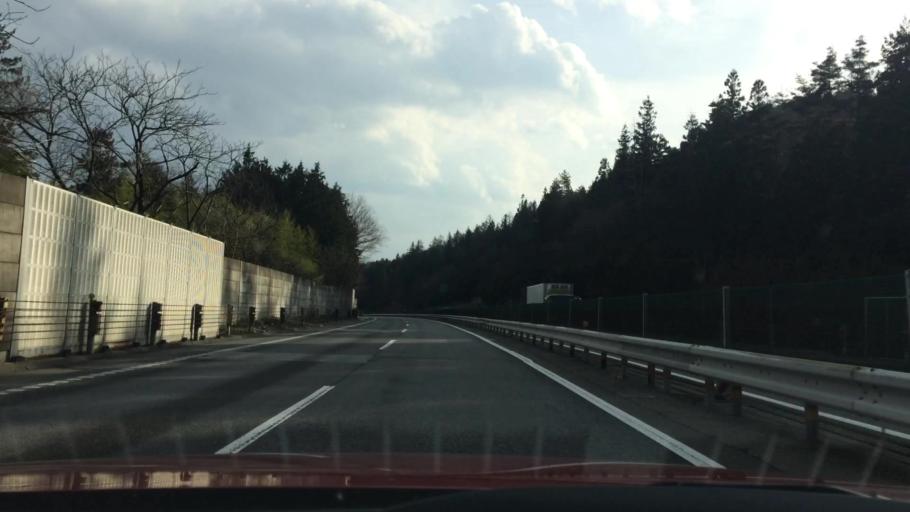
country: JP
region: Nagano
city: Ina
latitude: 35.7984
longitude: 137.9296
